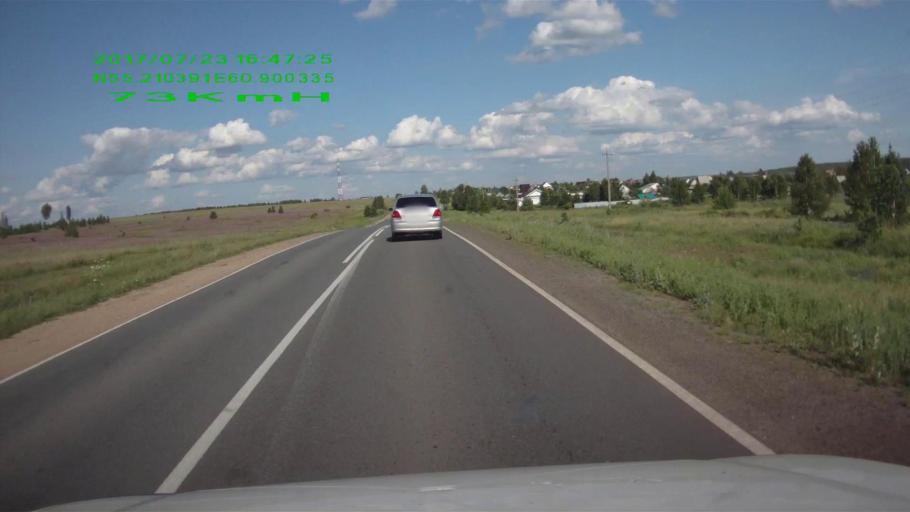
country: RU
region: Chelyabinsk
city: Poletayevo
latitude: 55.2104
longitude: 60.9002
